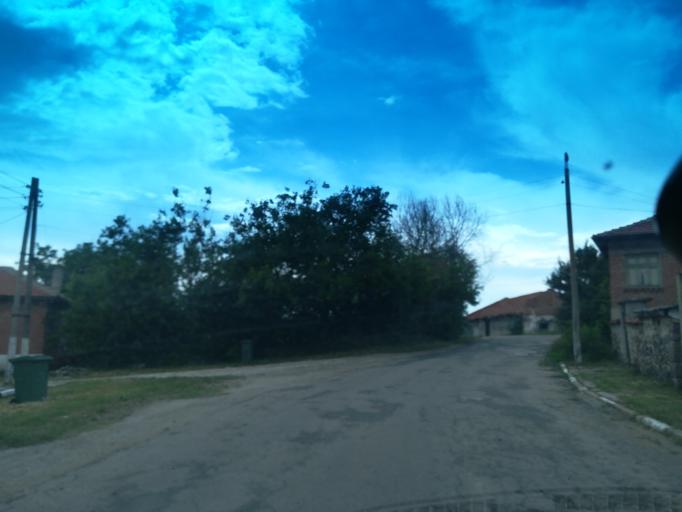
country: BG
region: Khaskovo
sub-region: Obshtina Mineralni Bani
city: Mineralni Bani
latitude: 41.9958
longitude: 25.2260
